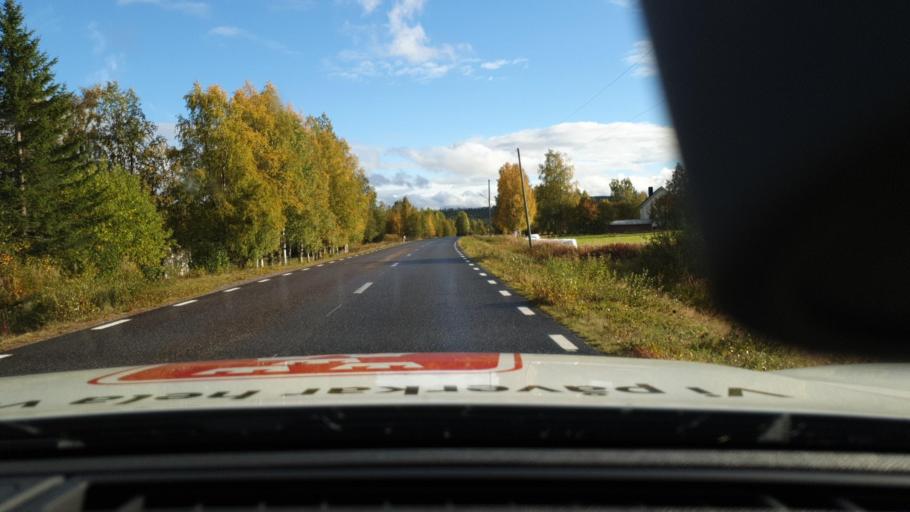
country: SE
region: Norrbotten
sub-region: Overkalix Kommun
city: OEverkalix
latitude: 66.9352
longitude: 22.7351
